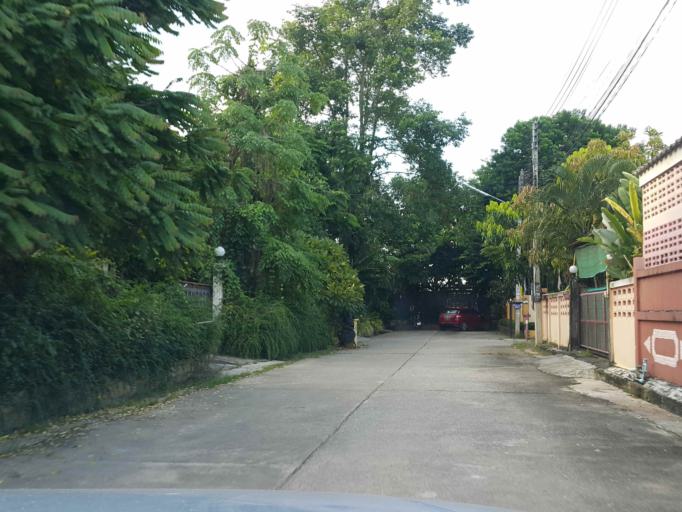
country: TH
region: Chiang Mai
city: San Sai
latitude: 18.9258
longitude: 98.9783
